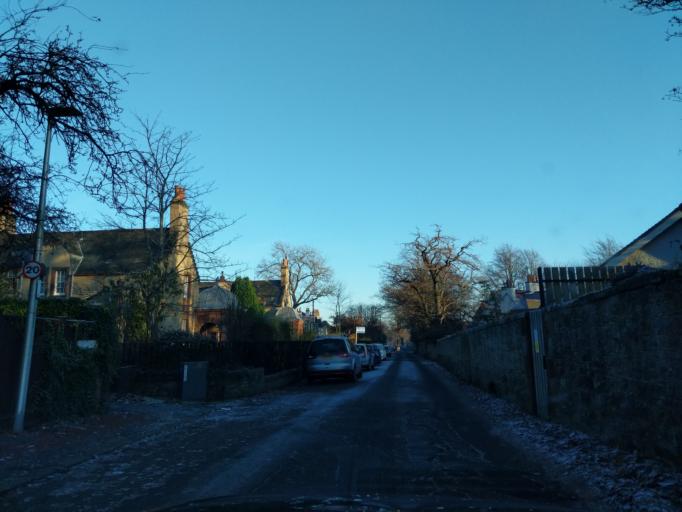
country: GB
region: Scotland
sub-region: Edinburgh
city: Colinton
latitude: 55.9091
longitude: -3.2638
